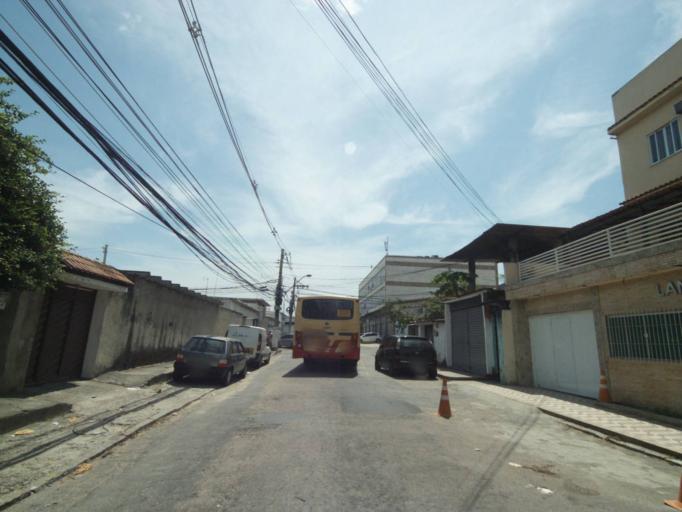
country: BR
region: Rio de Janeiro
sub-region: Duque De Caxias
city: Duque de Caxias
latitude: -22.7977
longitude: -43.2926
